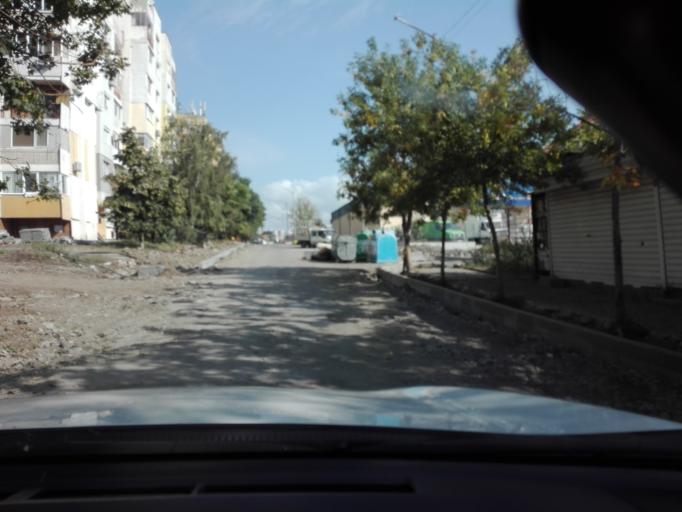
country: BG
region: Burgas
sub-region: Obshtina Burgas
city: Burgas
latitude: 42.4493
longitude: 27.4129
